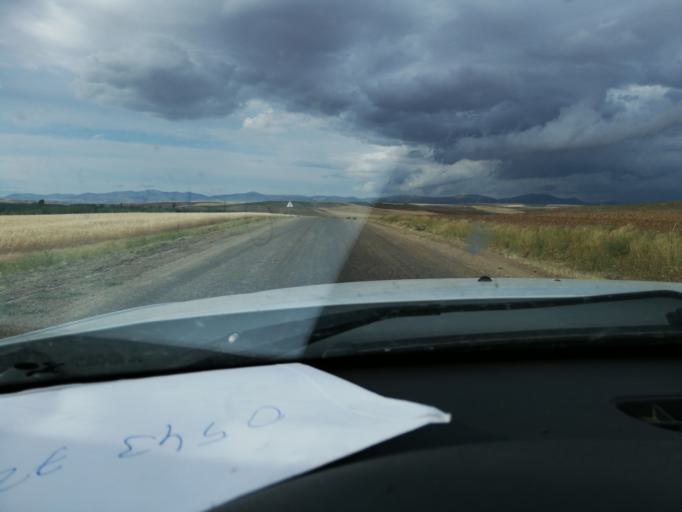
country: TR
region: Kirsehir
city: Kirsehir
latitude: 39.0335
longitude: 34.1418
